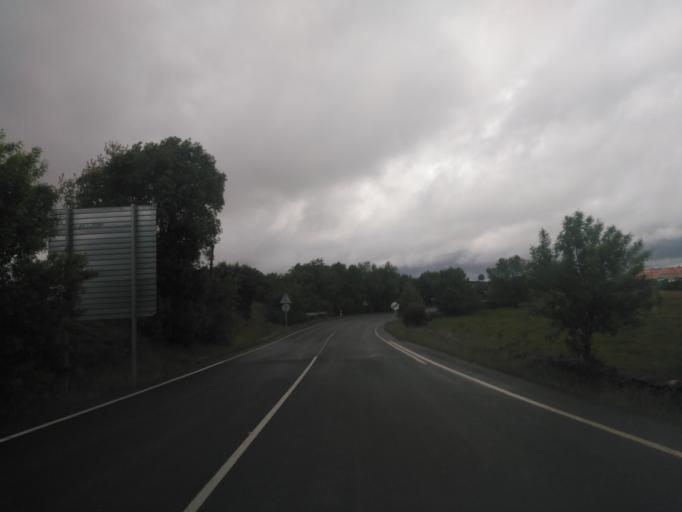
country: ES
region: Castille and Leon
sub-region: Provincia de Salamanca
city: Fuentes de Bejar
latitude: 40.5252
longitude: -5.6741
